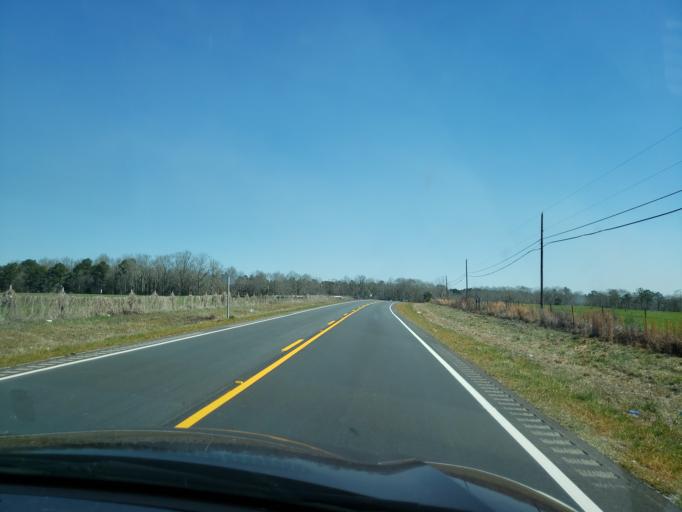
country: US
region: Alabama
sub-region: Macon County
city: Tuskegee
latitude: 32.5822
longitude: -85.7321
